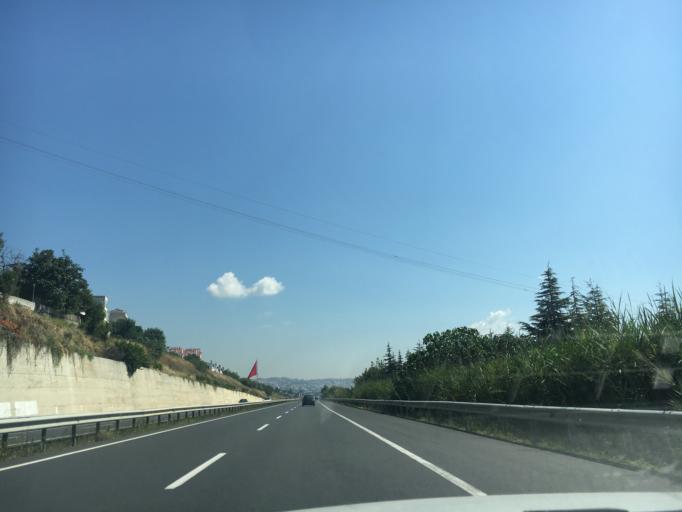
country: TR
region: Tekirdag
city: Sultankoy
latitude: 41.0243
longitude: 27.9973
